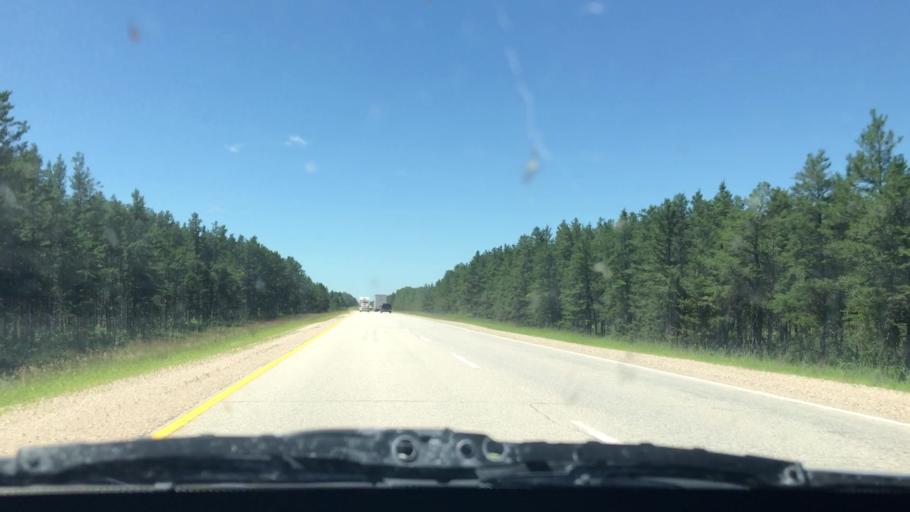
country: CA
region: Manitoba
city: La Broquerie
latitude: 49.6568
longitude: -96.1819
